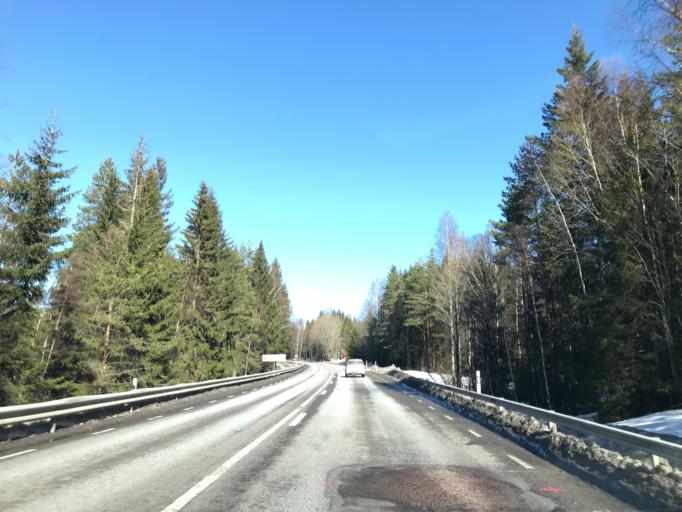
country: SE
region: Vaermland
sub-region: Filipstads Kommun
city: Filipstad
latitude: 59.7592
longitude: 14.2559
